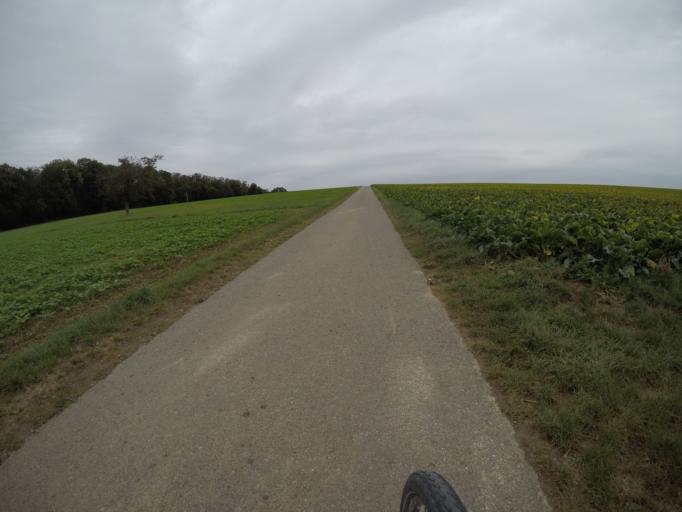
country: DE
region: Baden-Wuerttemberg
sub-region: Regierungsbezirk Stuttgart
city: Eberdingen
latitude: 48.8754
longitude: 8.9862
